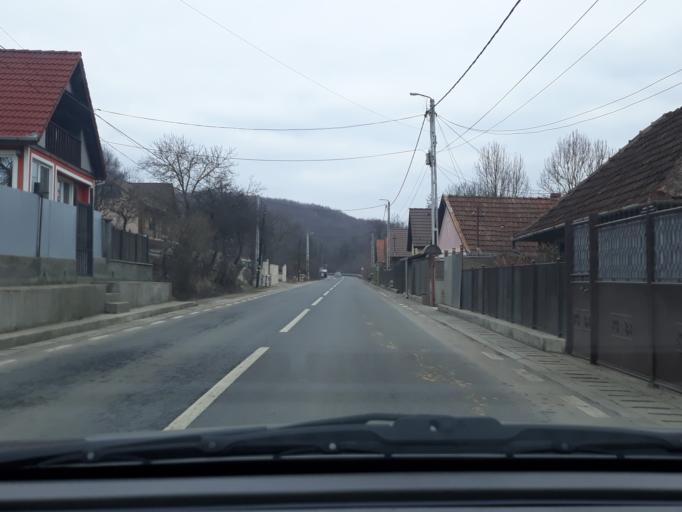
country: RO
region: Bihor
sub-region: Oras Alesd
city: Pestis
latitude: 47.0765
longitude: 22.4124
